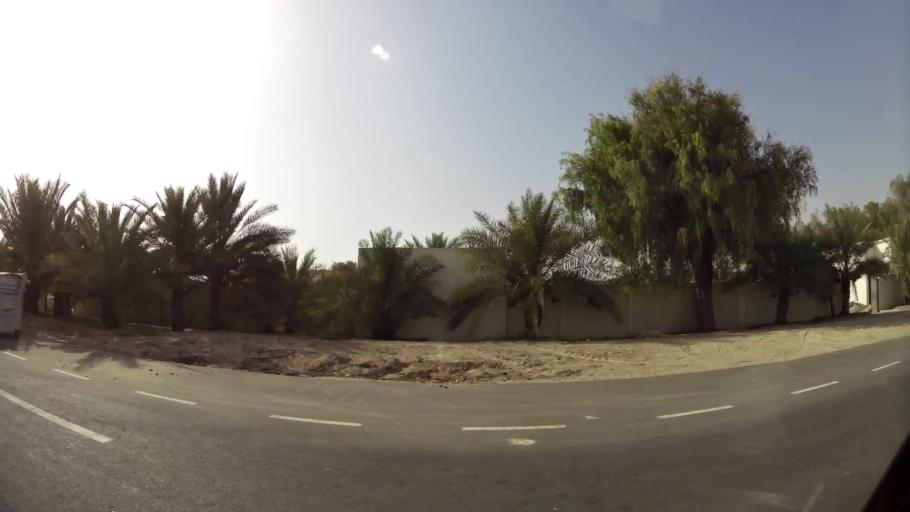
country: AE
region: Dubai
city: Dubai
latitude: 25.1458
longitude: 55.3222
